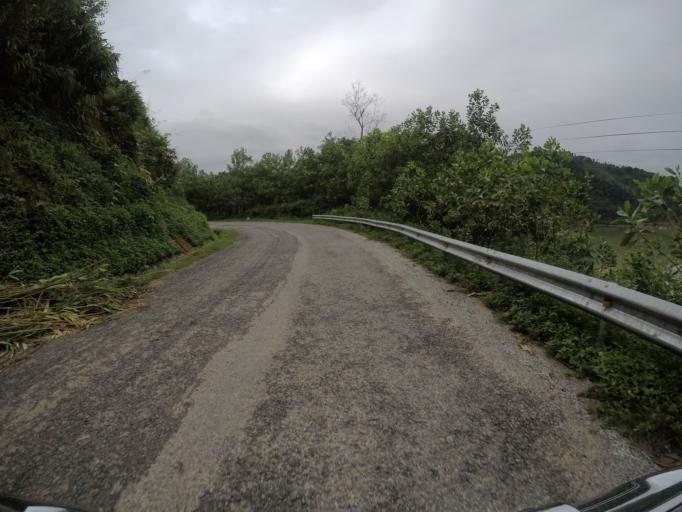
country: VN
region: Quang Nam
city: Thanh My
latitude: 15.6670
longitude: 107.6346
